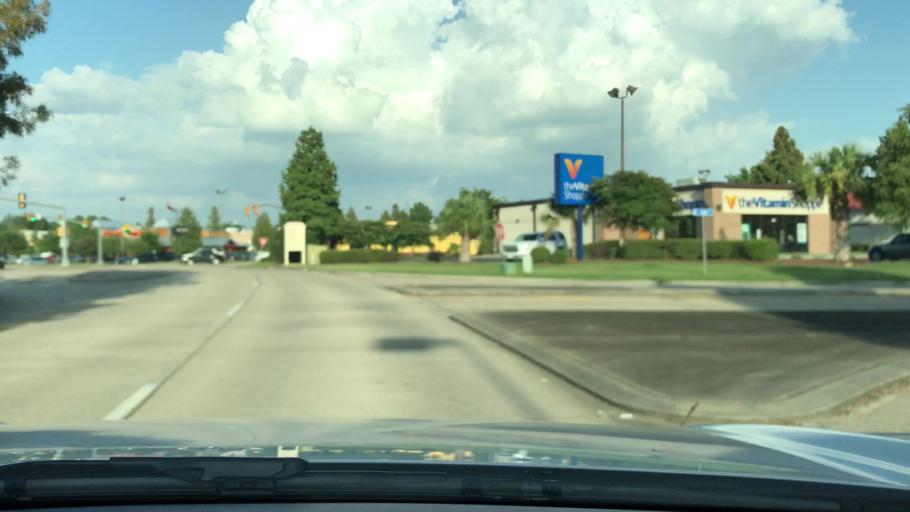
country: US
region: Louisiana
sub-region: East Baton Rouge Parish
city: Village Saint George
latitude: 30.3792
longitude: -91.0667
